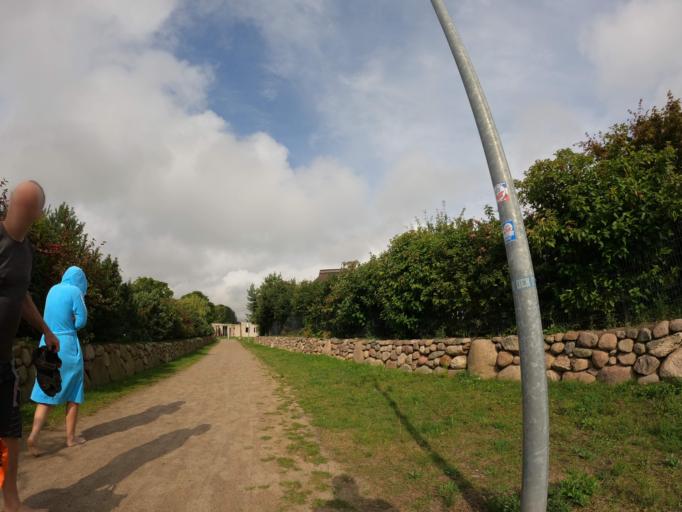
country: DE
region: Mecklenburg-Vorpommern
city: Ostseebad Gohren
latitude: 54.3211
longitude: 13.7291
